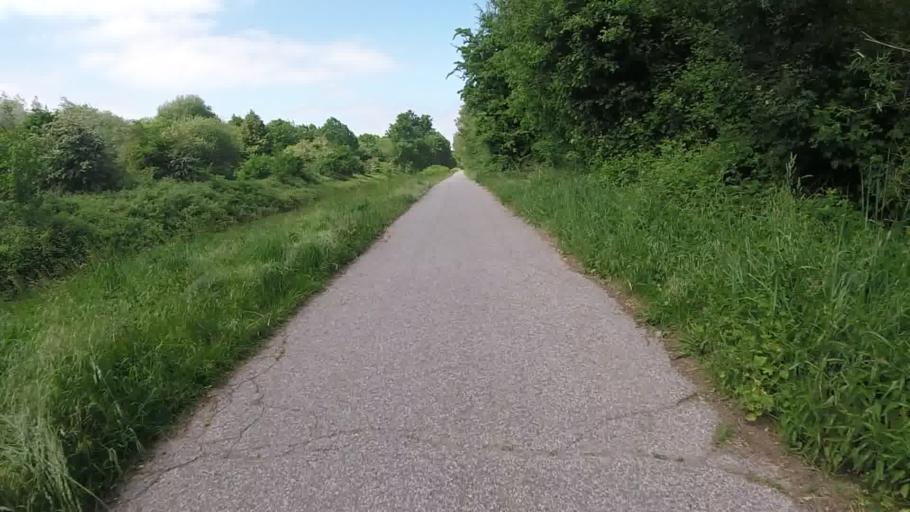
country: DE
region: Schleswig-Holstein
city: Oststeinbek
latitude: 53.4939
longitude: 10.1432
